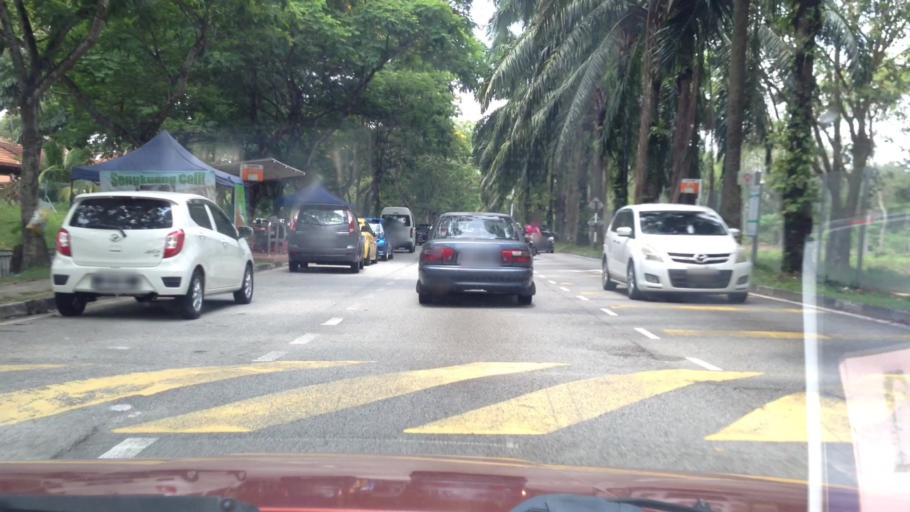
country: MY
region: Selangor
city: Kampung Baru Subang
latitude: 3.1716
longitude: 101.5502
